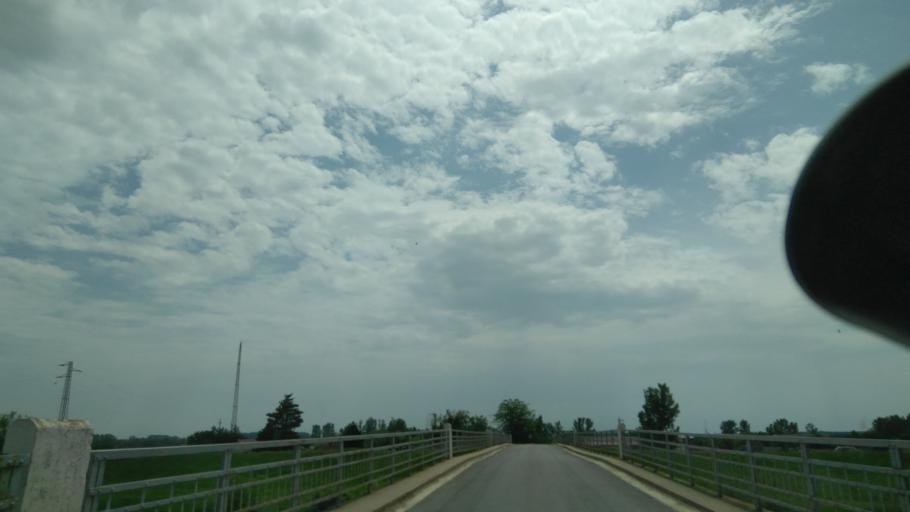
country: HU
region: Hajdu-Bihar
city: Komadi
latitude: 47.0118
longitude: 21.6060
